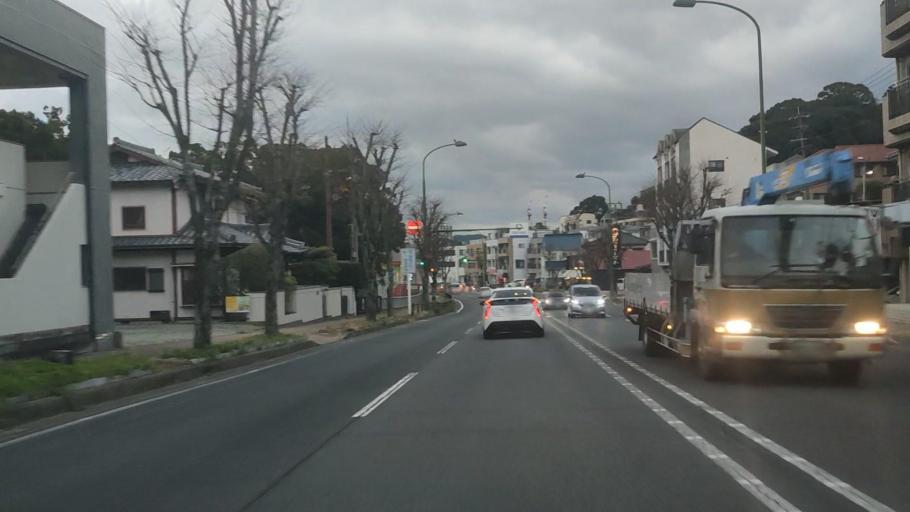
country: JP
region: Nagasaki
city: Nagasaki-shi
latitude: 32.7604
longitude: 129.8876
